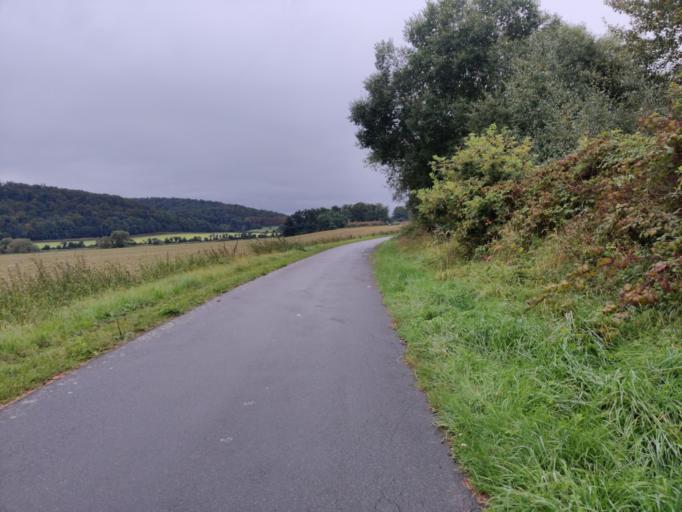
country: DE
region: Lower Saxony
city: Furstenberg
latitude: 51.7325
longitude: 9.3876
